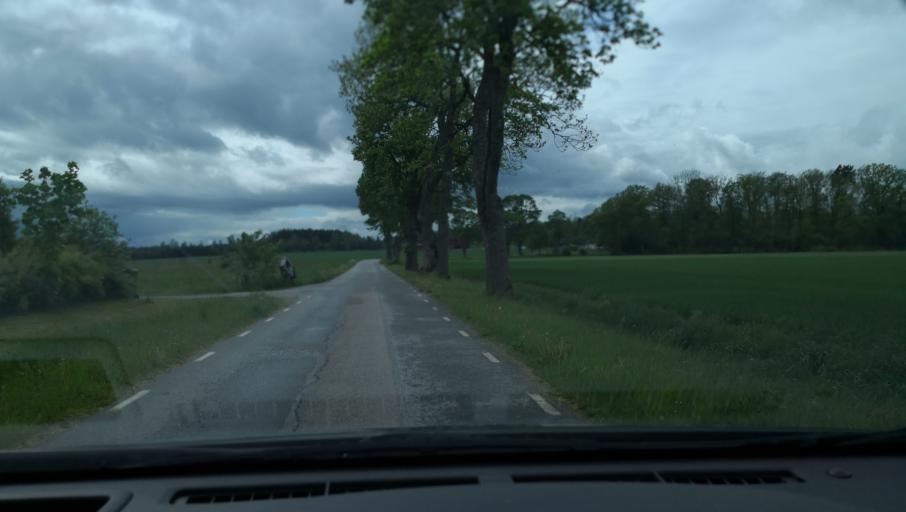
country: SE
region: Uppsala
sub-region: Enkopings Kommun
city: Orsundsbro
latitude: 59.7237
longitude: 17.4042
